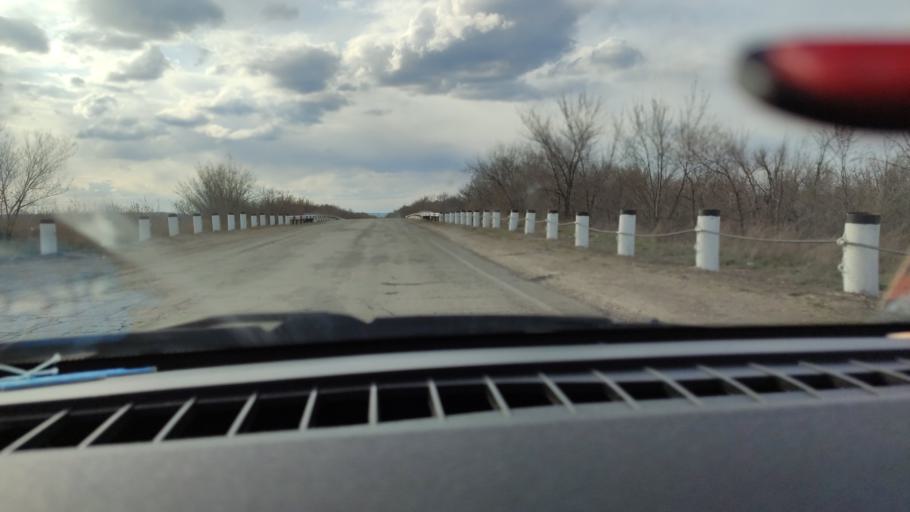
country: RU
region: Saratov
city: Krasnoarmeysk
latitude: 51.0760
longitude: 45.9762
